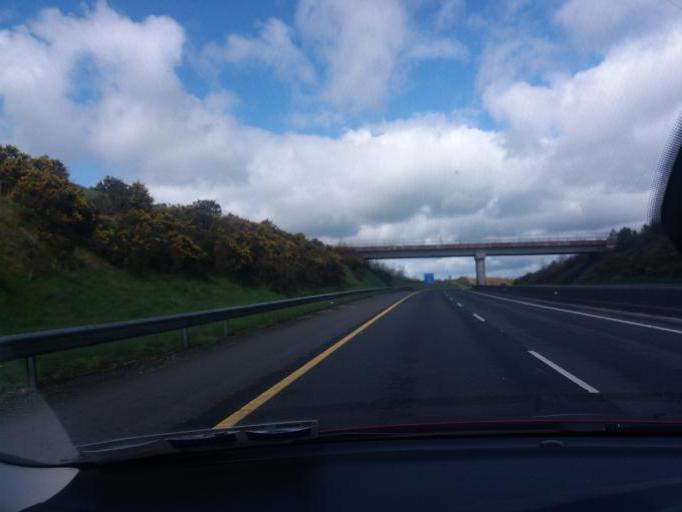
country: IE
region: Munster
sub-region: County Cork
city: Mitchelstown
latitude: 52.2168
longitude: -8.2818
